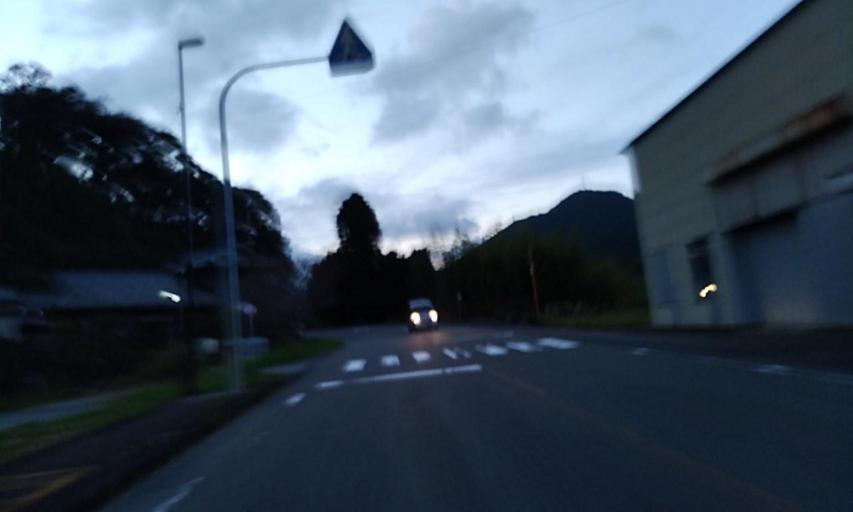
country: JP
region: Wakayama
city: Shingu
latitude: 33.7225
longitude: 135.9677
